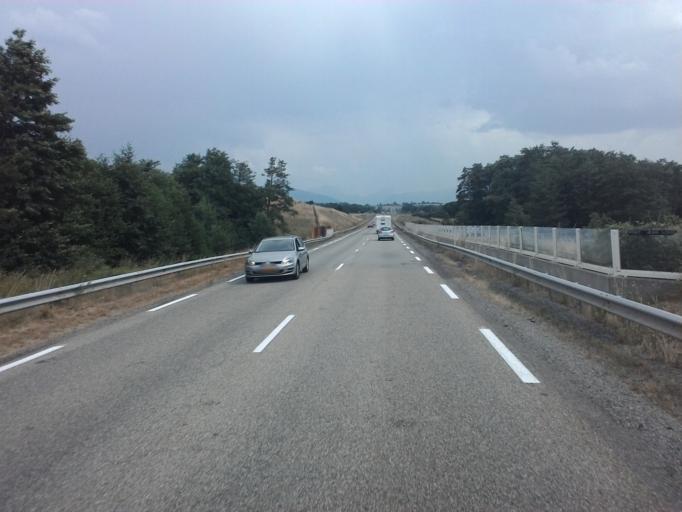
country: FR
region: Rhone-Alpes
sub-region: Departement de l'Isere
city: Pierre-Chatel
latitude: 44.9649
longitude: 5.7769
